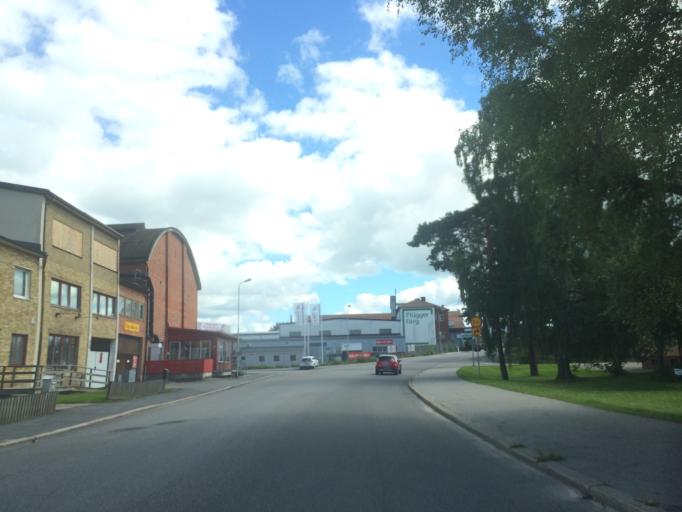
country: SE
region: Vaestra Goetaland
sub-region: Trollhattan
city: Trollhattan
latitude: 58.2833
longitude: 12.3008
